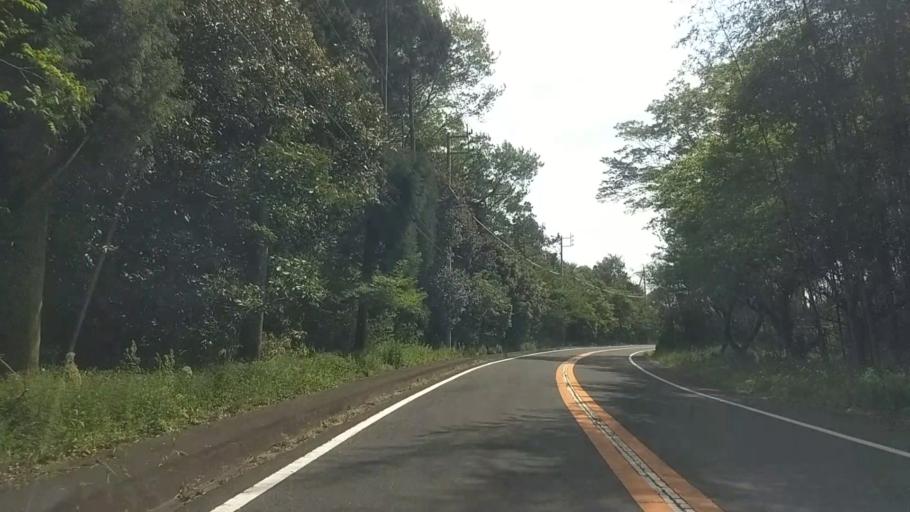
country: JP
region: Shizuoka
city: Kosai-shi
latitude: 34.7360
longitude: 137.6001
